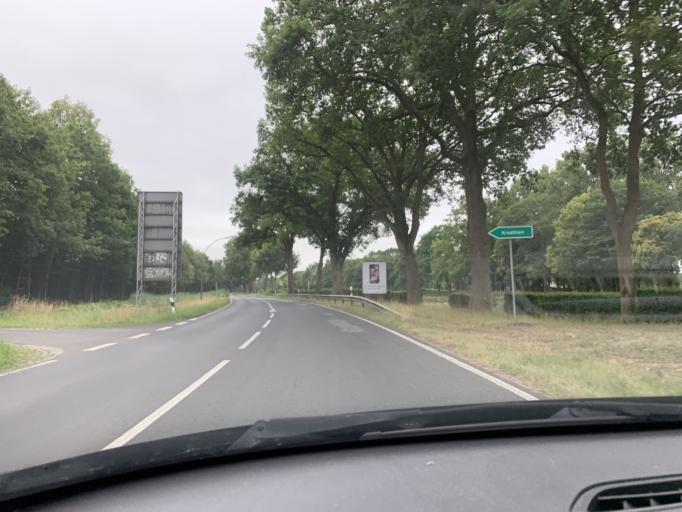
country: DE
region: Lower Saxony
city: Lingen
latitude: 52.4913
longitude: 7.2958
